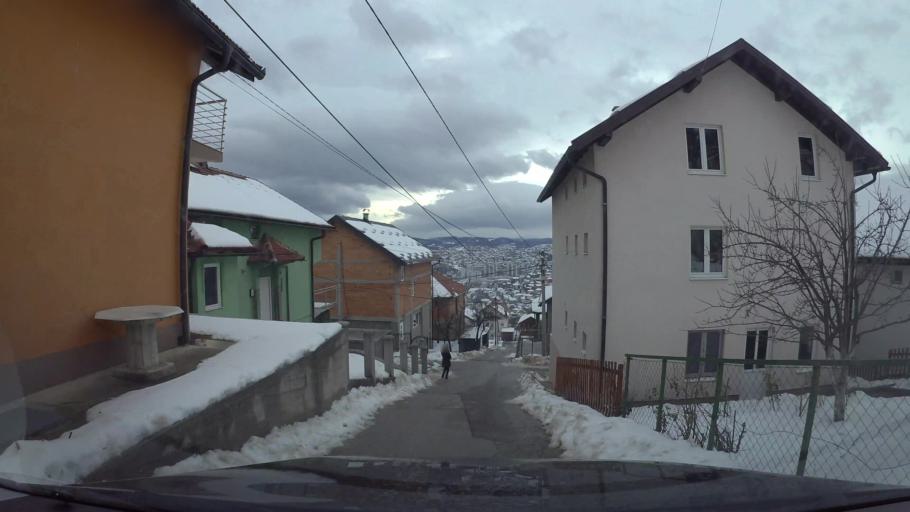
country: BA
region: Federation of Bosnia and Herzegovina
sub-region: Kanton Sarajevo
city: Sarajevo
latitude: 43.8650
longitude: 18.3617
